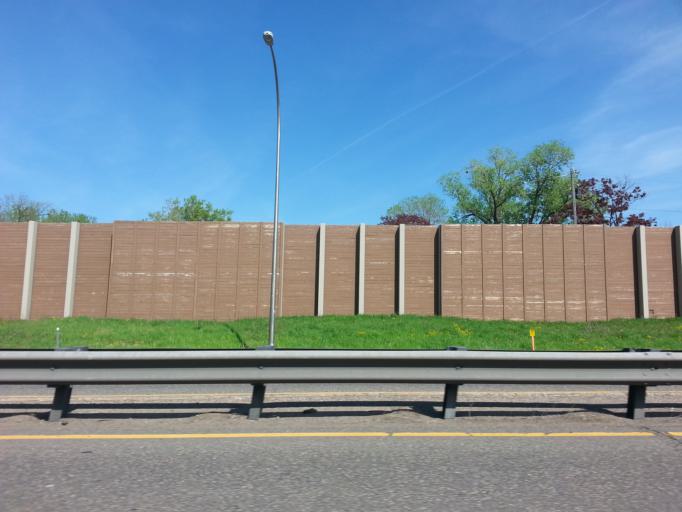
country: US
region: Minnesota
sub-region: Ramsey County
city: Lauderdale
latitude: 44.9981
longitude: -93.2062
